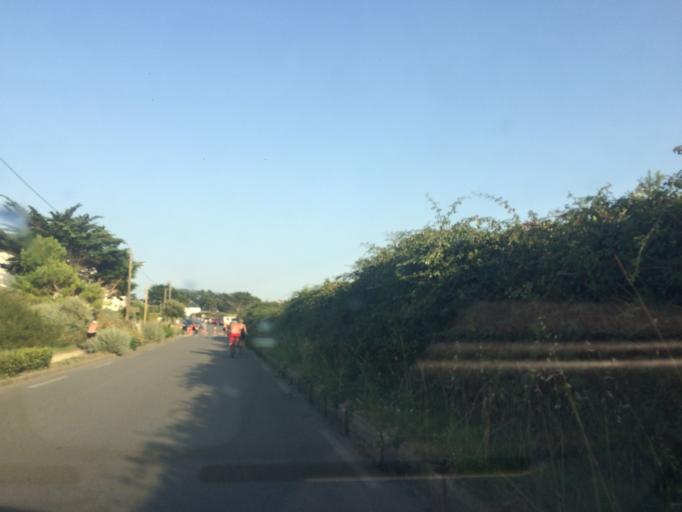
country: FR
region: Brittany
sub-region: Departement du Morbihan
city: Damgan
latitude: 47.5136
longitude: -2.5577
